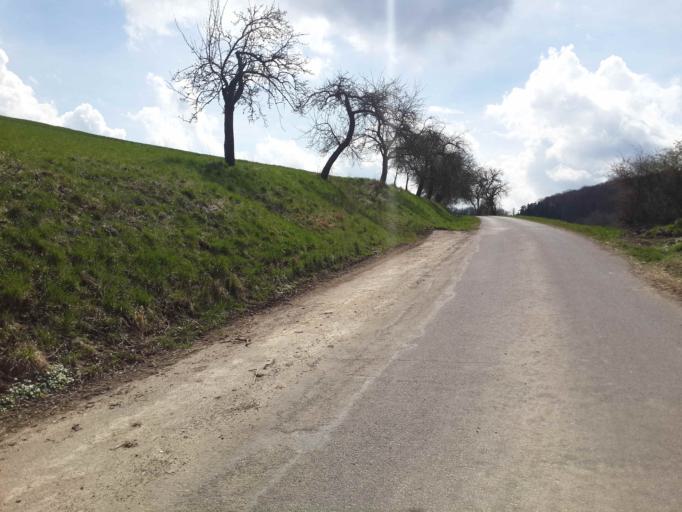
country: DE
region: Baden-Wuerttemberg
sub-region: Regierungsbezirk Stuttgart
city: Bad Mergentheim
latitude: 49.4391
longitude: 9.7460
